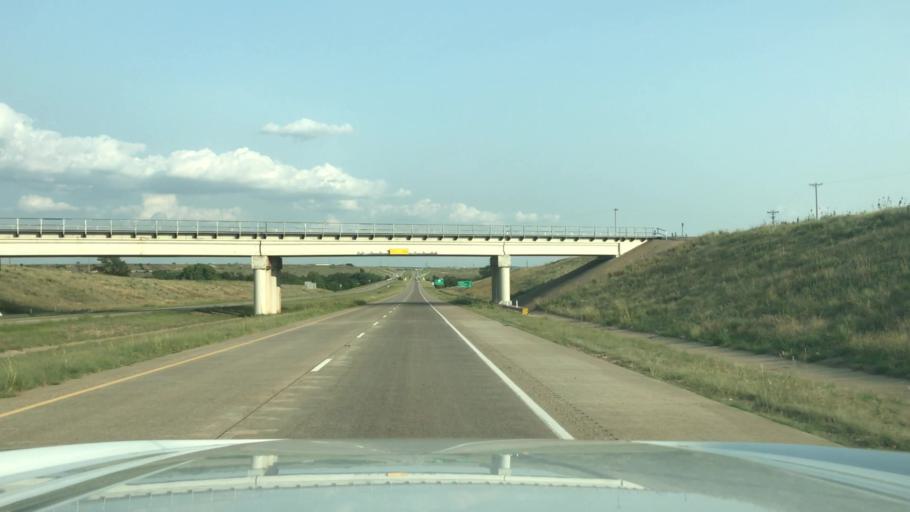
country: US
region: Texas
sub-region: Randall County
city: Canyon
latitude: 35.0135
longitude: -101.9106
